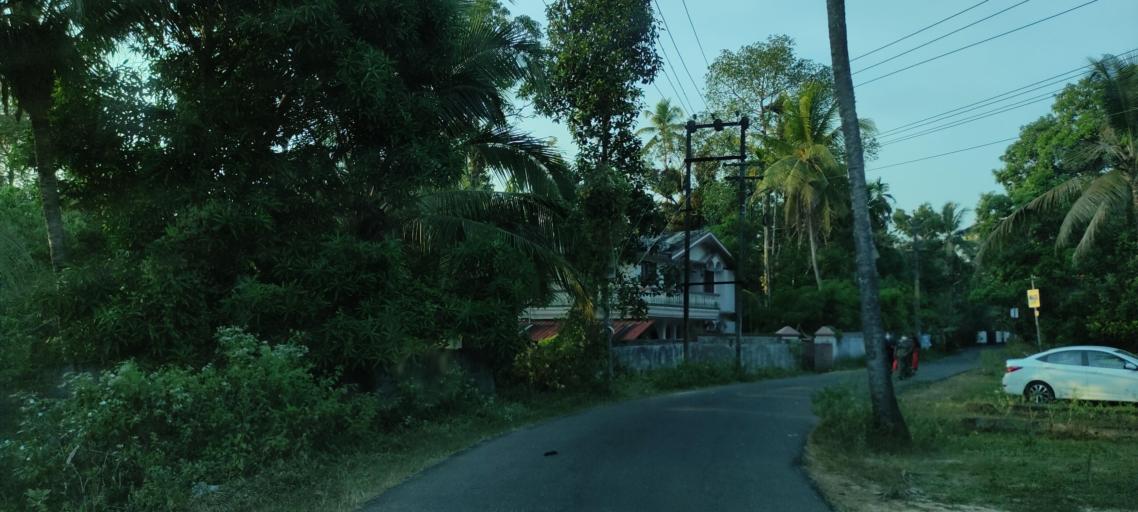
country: IN
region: Kerala
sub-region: Alappuzha
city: Kutiatodu
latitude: 9.7737
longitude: 76.3254
